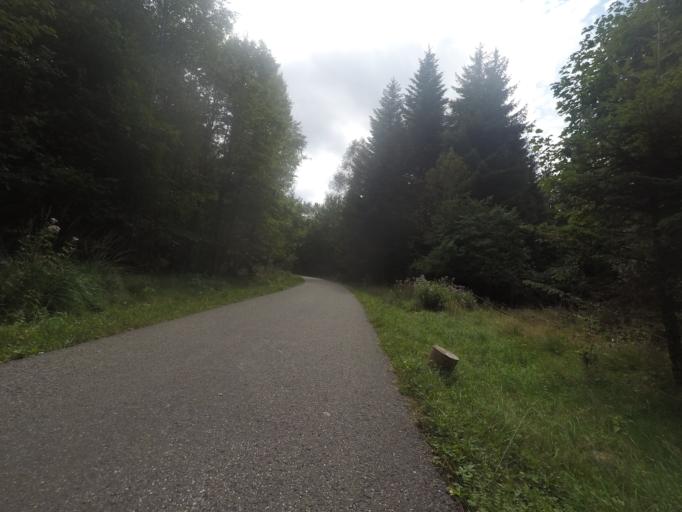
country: DE
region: Baden-Wuerttemberg
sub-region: Karlsruhe Region
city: Dobel
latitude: 48.7825
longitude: 8.4695
